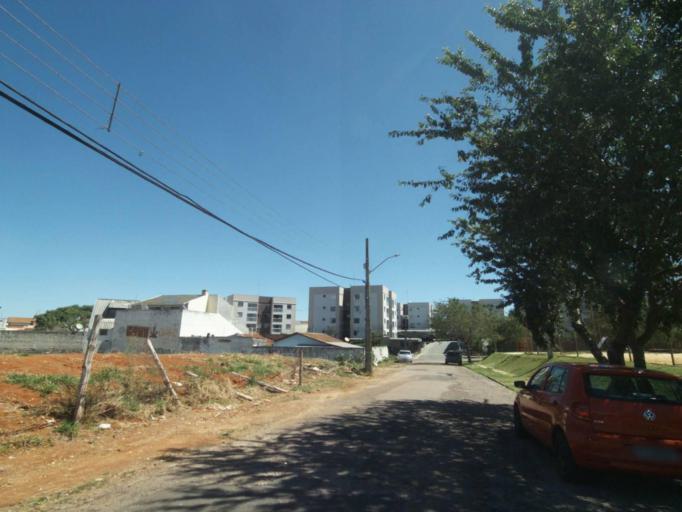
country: BR
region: Parana
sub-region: Curitiba
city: Curitiba
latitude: -25.4708
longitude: -49.3404
